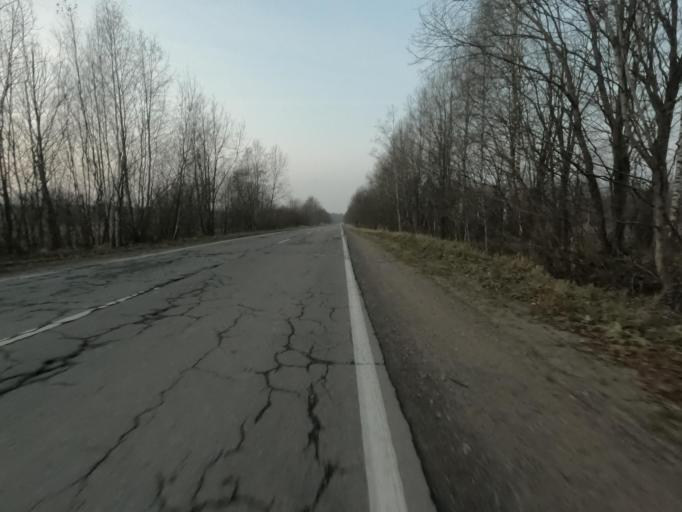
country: RU
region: Leningrad
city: Kirovsk
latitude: 59.8604
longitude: 30.9810
